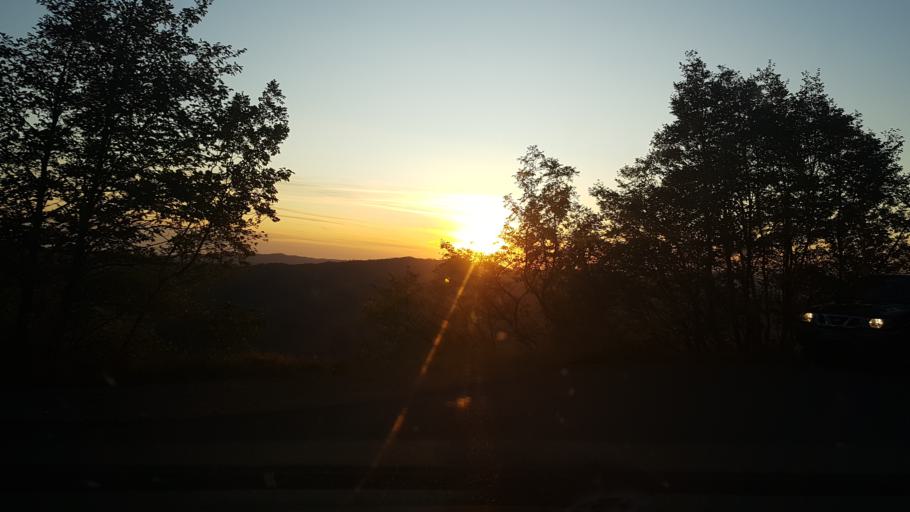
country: SI
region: Vipava
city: Vipava
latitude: 45.7925
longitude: 14.0105
